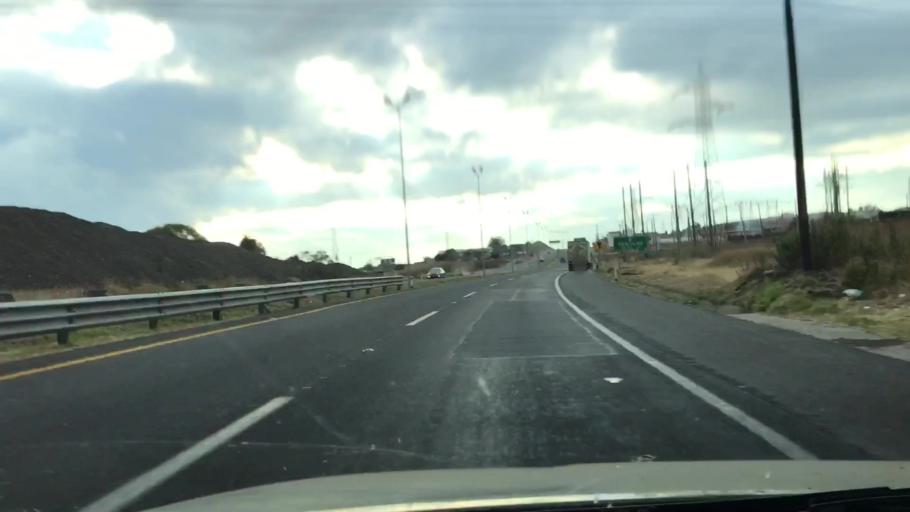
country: MX
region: Guanajuato
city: Penjamo
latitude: 20.4210
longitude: -101.7163
